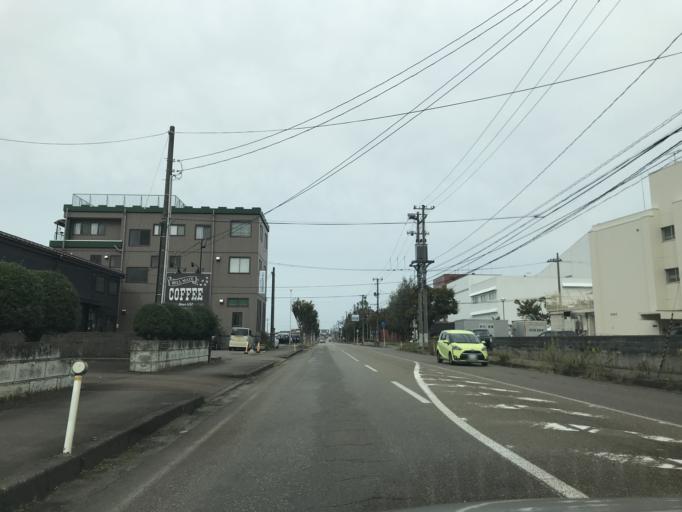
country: JP
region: Niigata
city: Nagaoka
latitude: 37.4341
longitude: 138.8377
